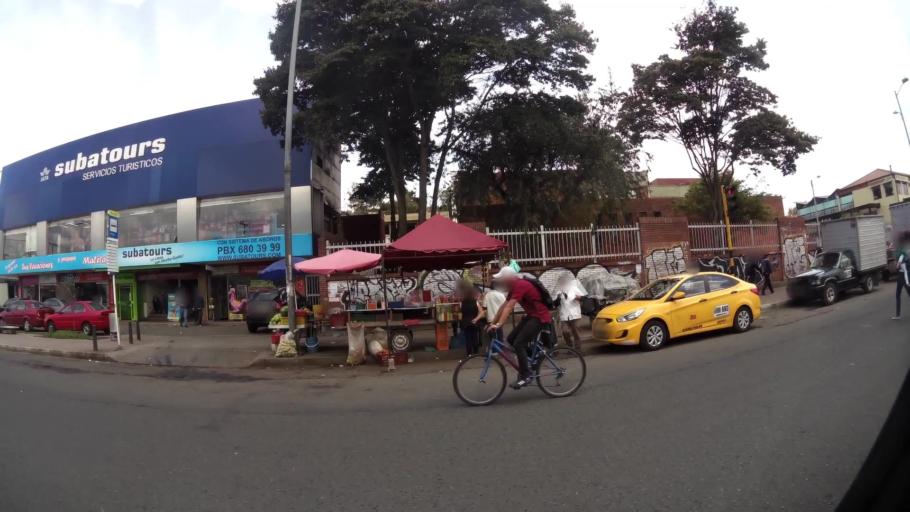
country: CO
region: Cundinamarca
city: Cota
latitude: 4.7429
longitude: -74.0847
